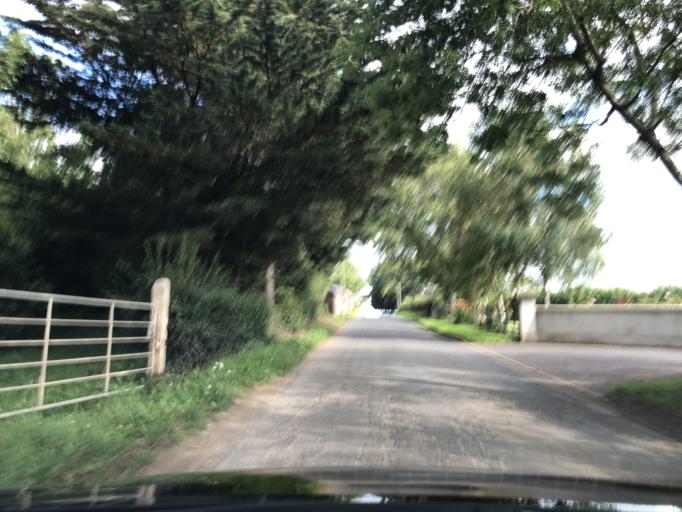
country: GB
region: Northern Ireland
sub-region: Ards District
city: Newtownards
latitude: 54.5609
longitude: -5.7091
